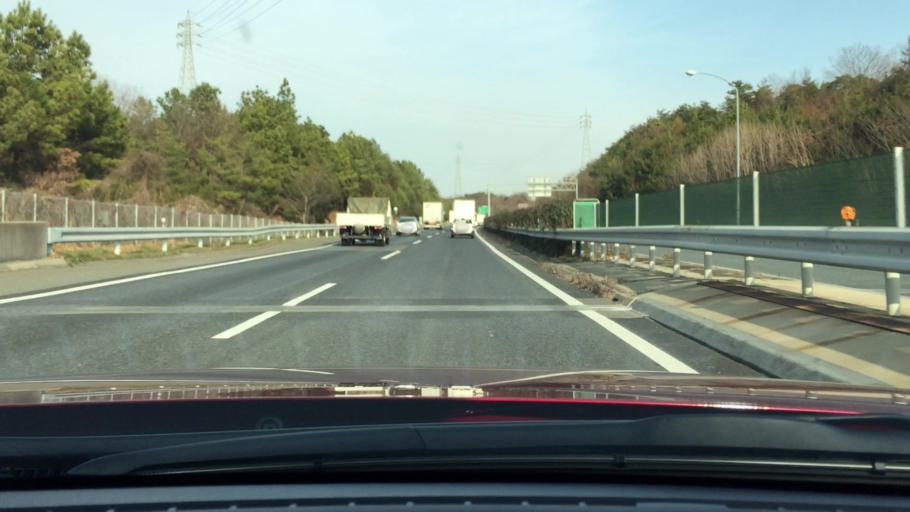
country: JP
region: Hyogo
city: Miki
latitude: 34.8147
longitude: 134.9622
